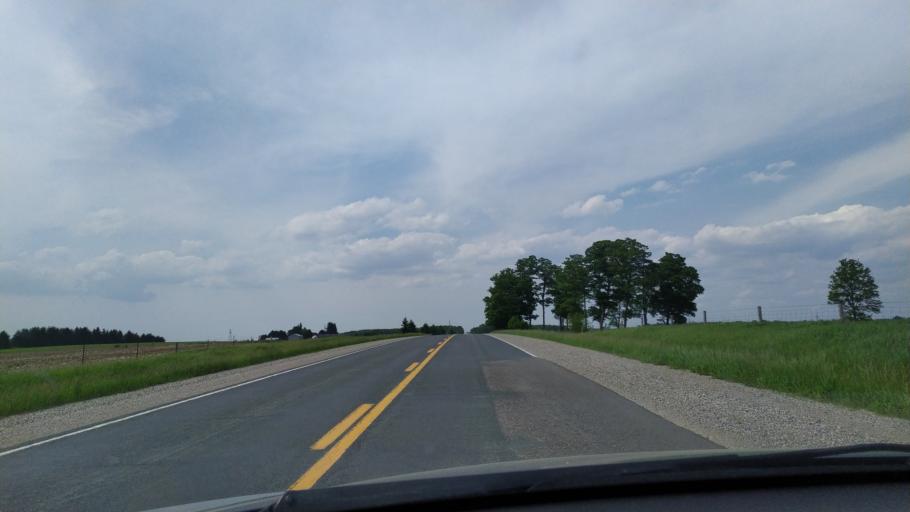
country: CA
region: Ontario
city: Ingersoll
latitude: 43.0306
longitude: -80.9732
